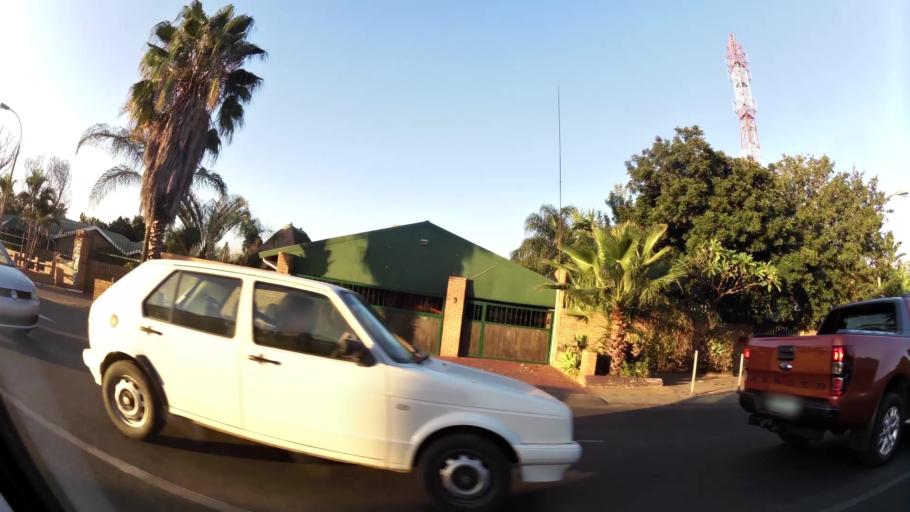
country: ZA
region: North-West
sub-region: Bojanala Platinum District Municipality
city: Rustenburg
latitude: -25.6933
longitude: 27.2249
